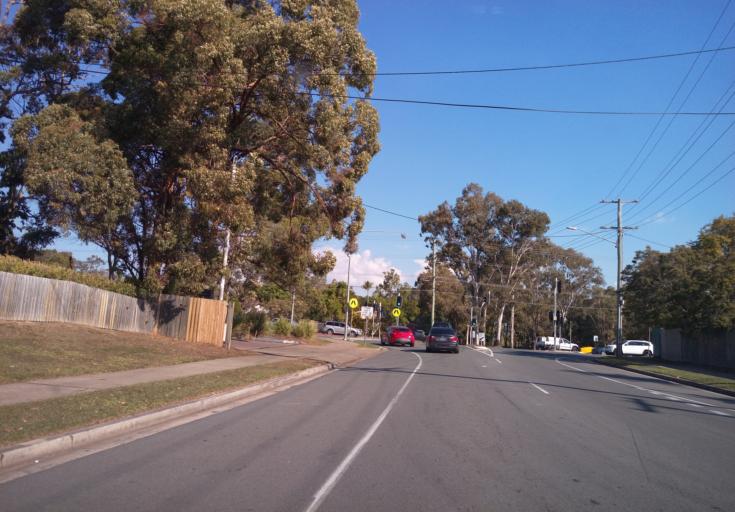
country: AU
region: Queensland
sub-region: Redland
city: Wellington Point
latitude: -27.5208
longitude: 153.2116
